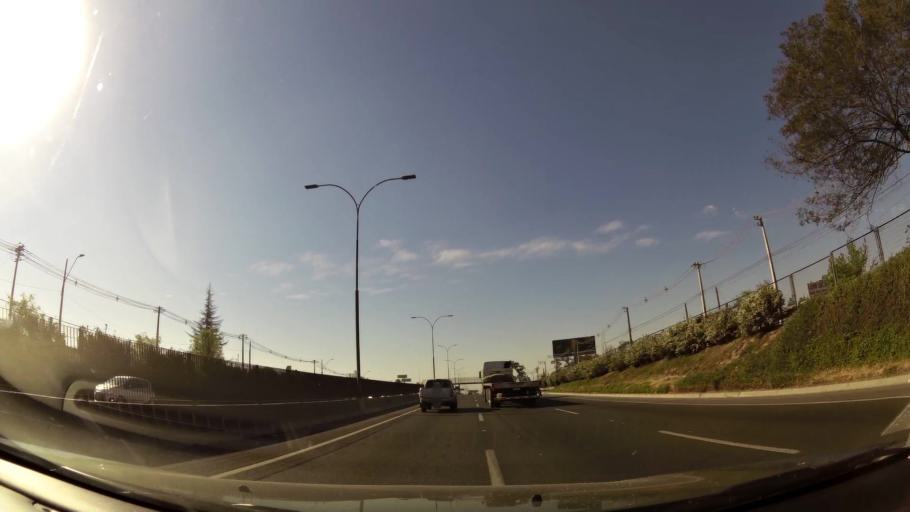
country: CL
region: Santiago Metropolitan
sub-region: Provincia de Maipo
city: San Bernardo
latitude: -33.5727
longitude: -70.7125
